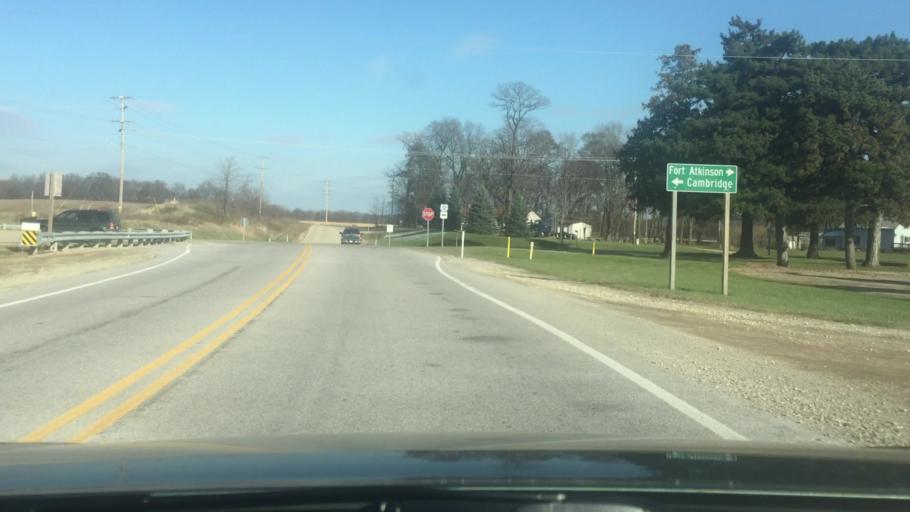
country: US
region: Wisconsin
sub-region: Jefferson County
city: Fort Atkinson
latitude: 42.9491
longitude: -88.8784
